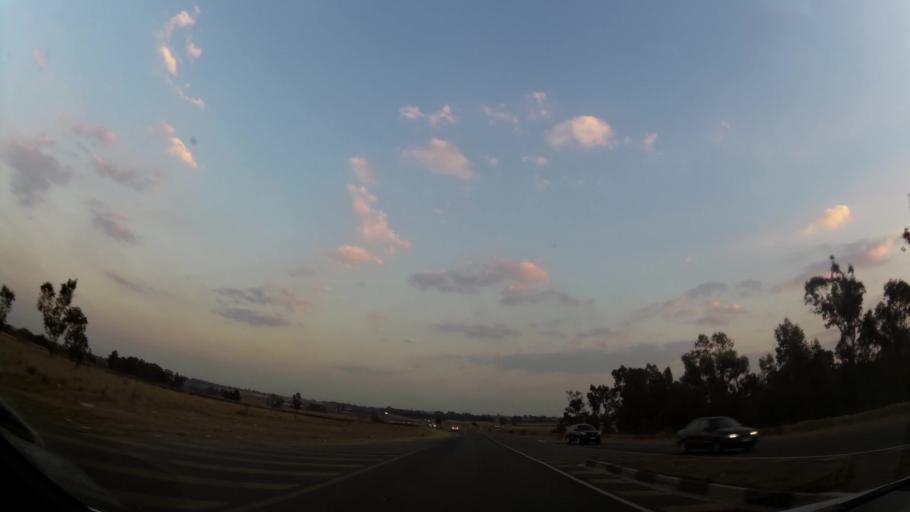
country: ZA
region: Gauteng
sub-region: Ekurhuleni Metropolitan Municipality
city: Springs
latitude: -26.2787
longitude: 28.4296
